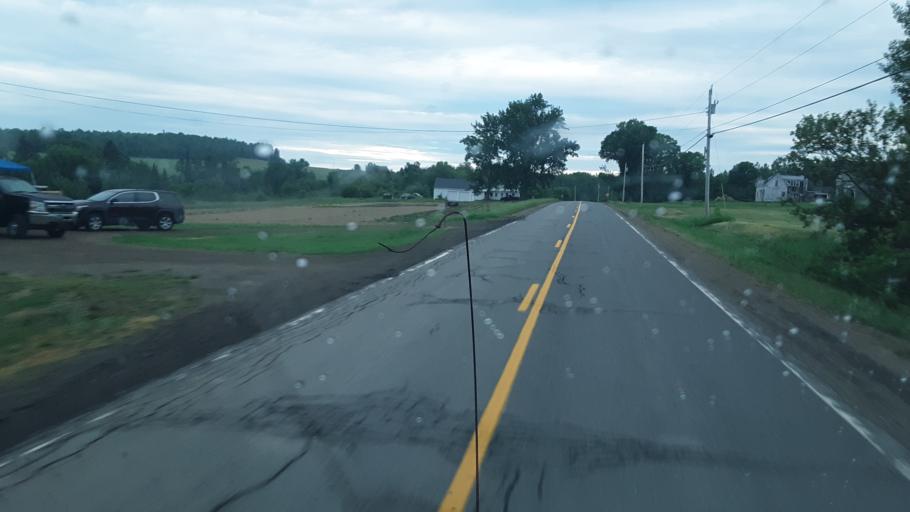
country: US
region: Maine
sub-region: Aroostook County
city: Presque Isle
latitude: 46.7325
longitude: -68.1979
